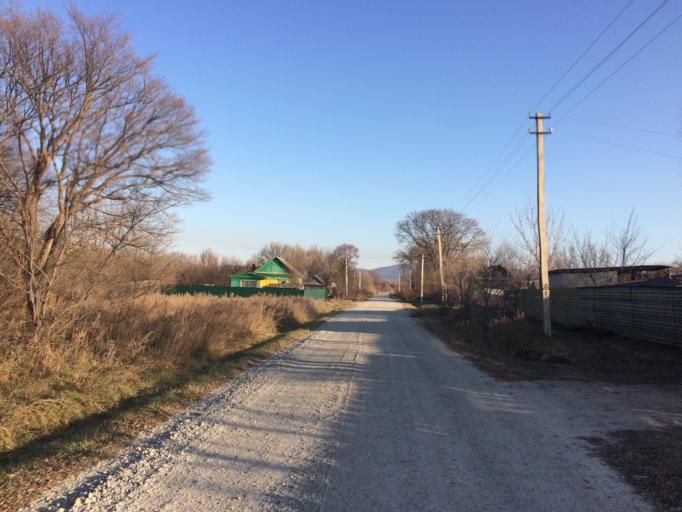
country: RU
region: Primorskiy
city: Ivanovka
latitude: 43.9568
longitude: 132.4798
